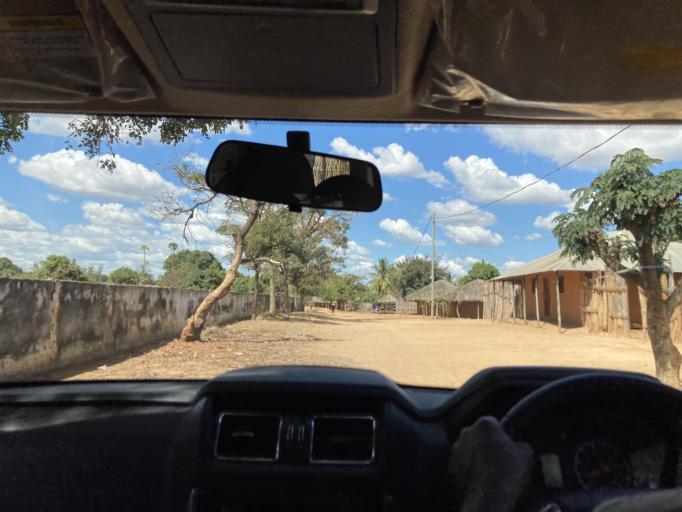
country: MZ
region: Cabo Delgado
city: Montepuez
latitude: -13.1442
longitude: 38.9820
